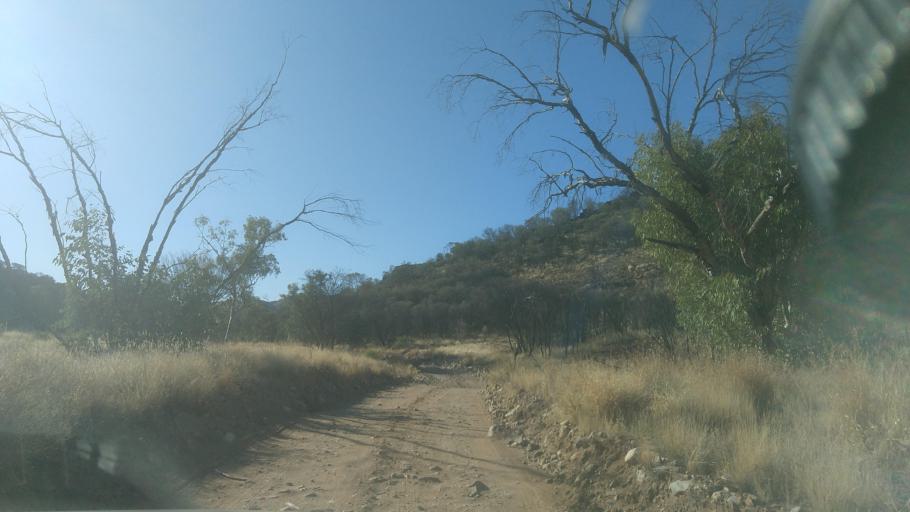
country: AU
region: Northern Territory
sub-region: Alice Springs
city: Alice Springs
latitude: -23.7474
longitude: 132.9135
